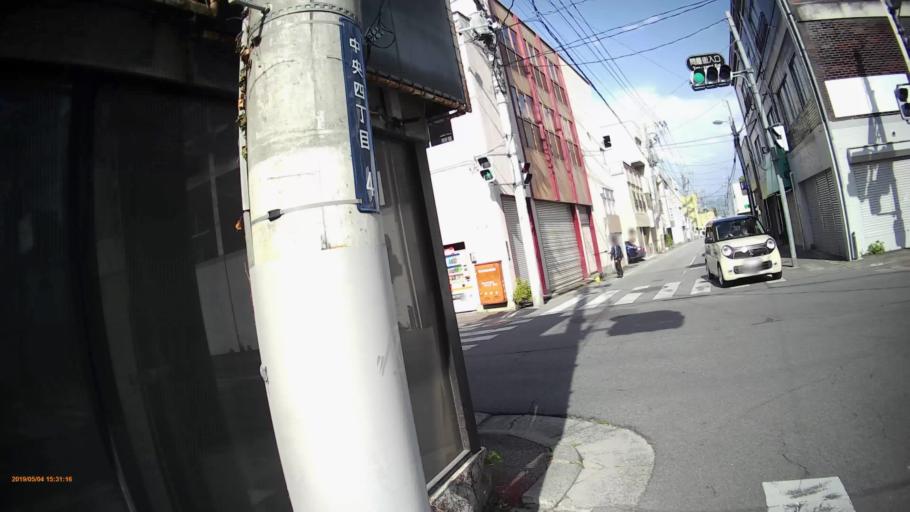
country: JP
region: Yamanashi
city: Kofu-shi
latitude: 35.6584
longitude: 138.5716
